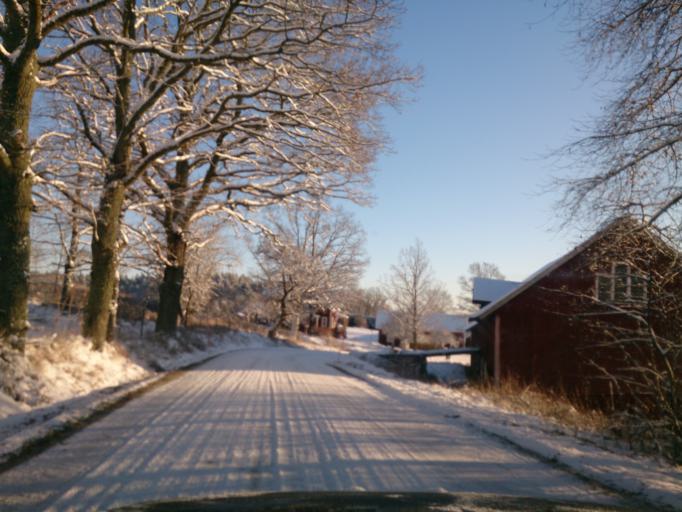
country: SE
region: OEstergoetland
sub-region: Norrkopings Kommun
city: Krokek
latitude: 58.5187
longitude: 16.5187
